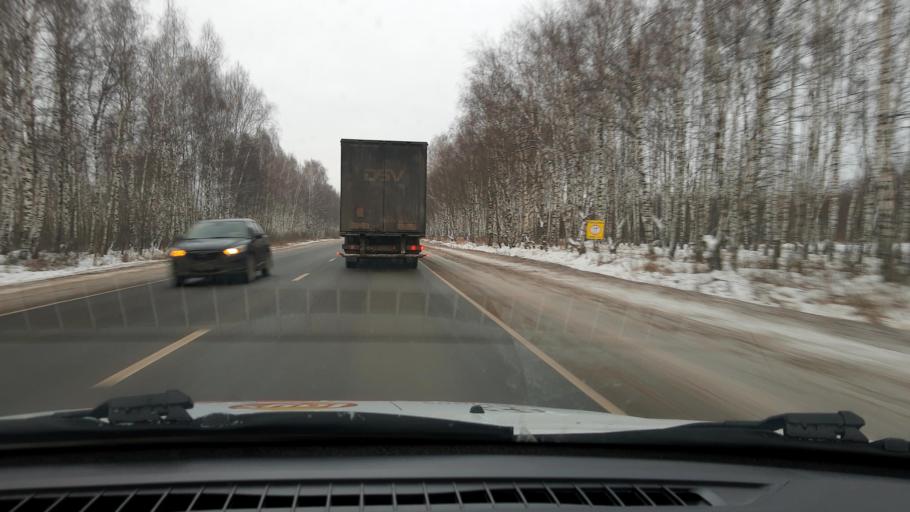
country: RU
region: Nizjnij Novgorod
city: Sitniki
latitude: 56.5169
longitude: 44.0250
